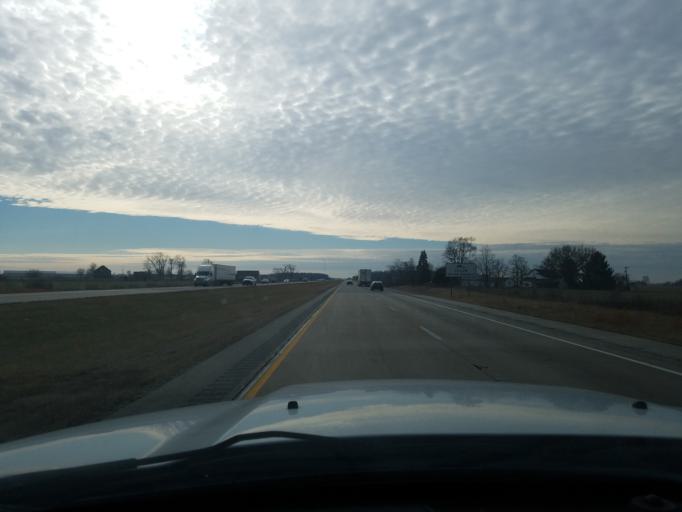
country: US
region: Indiana
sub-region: Huntington County
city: Markle
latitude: 40.7703
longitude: -85.3905
